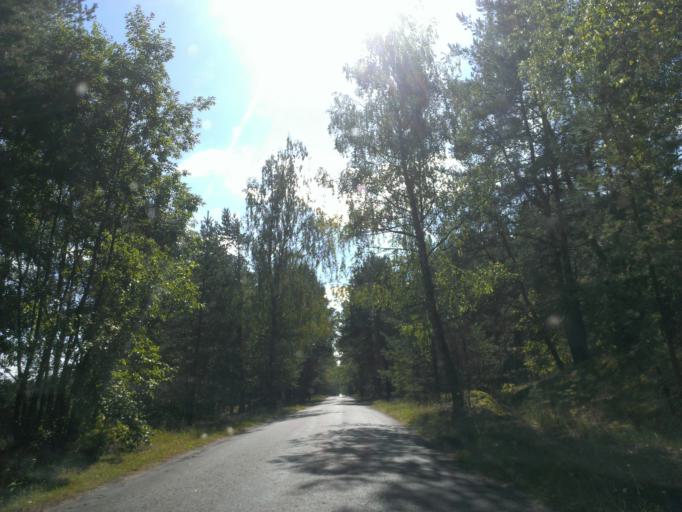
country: LV
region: Adazi
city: Adazi
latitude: 57.1113
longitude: 24.3458
